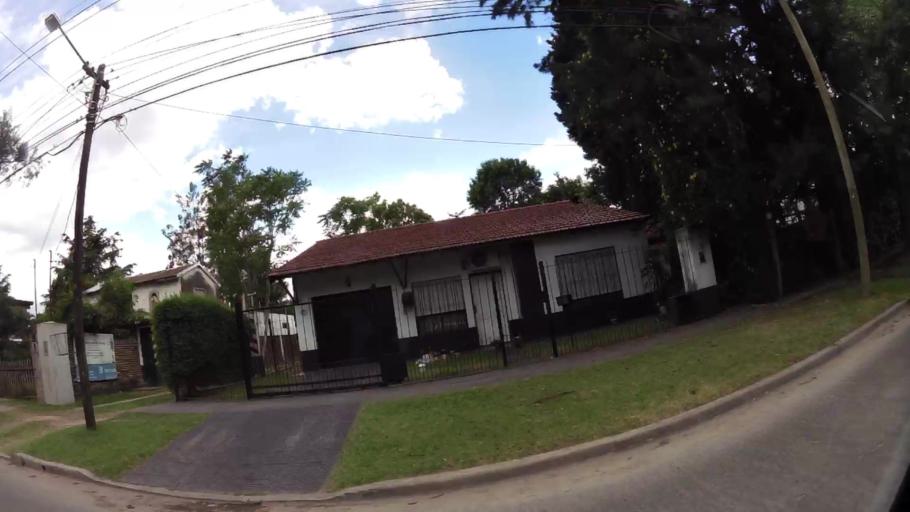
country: AR
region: Buenos Aires
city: Ituzaingo
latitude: -34.6350
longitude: -58.6800
